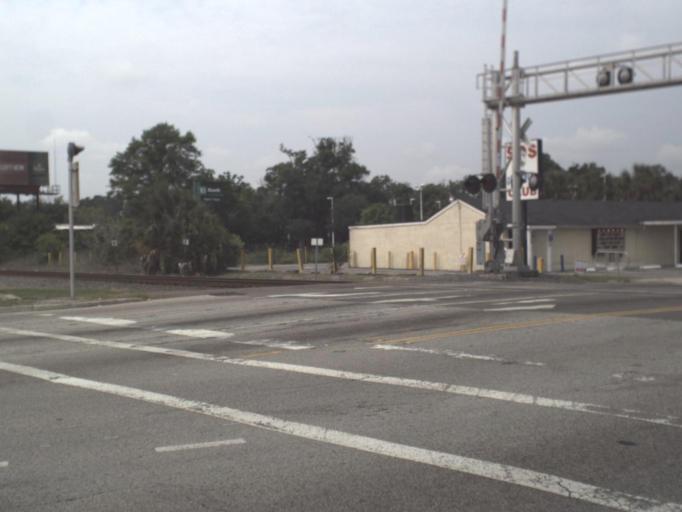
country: US
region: Florida
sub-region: Duval County
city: Jacksonville
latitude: 30.2823
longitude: -81.7204
